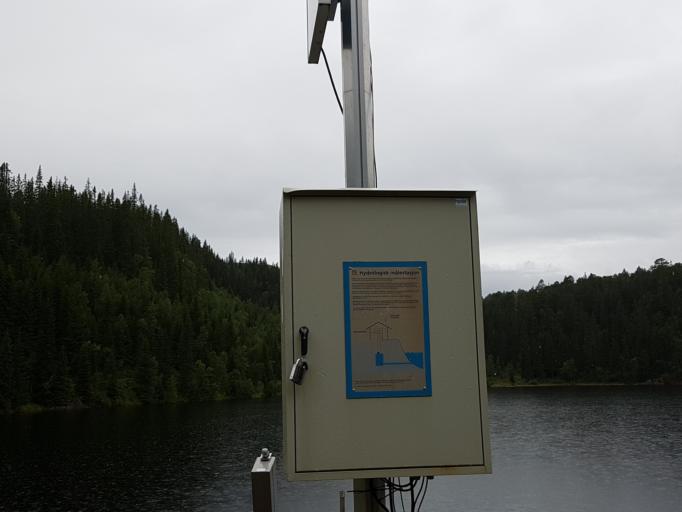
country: NO
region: Sor-Trondelag
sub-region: Trondheim
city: Trondheim
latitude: 63.4228
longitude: 10.2821
